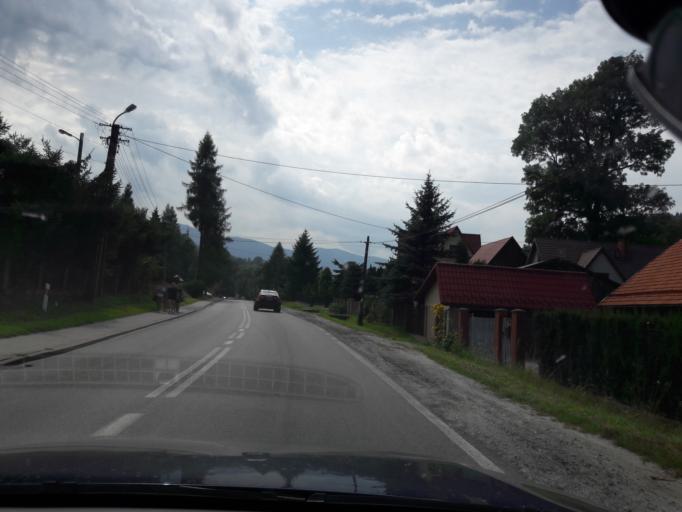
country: PL
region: Lesser Poland Voivodeship
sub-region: Powiat suski
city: Zawoja
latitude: 49.6540
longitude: 19.5506
